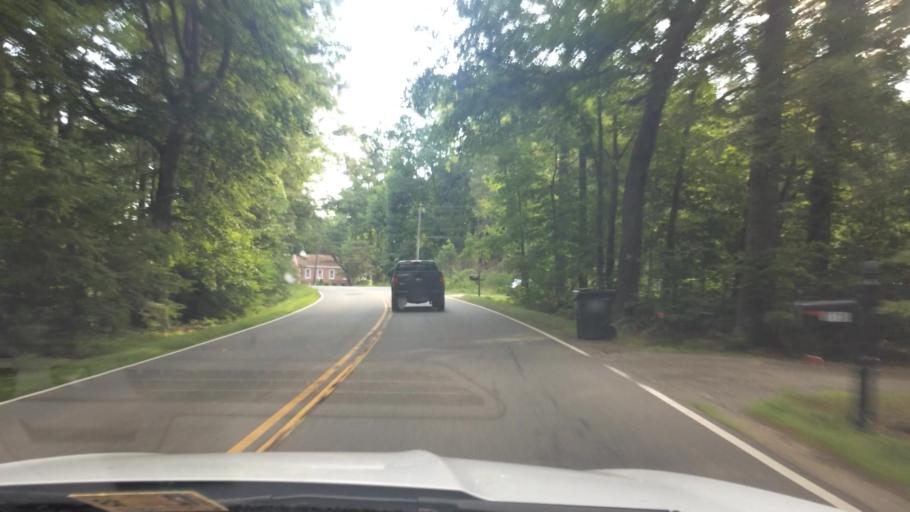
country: US
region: Virginia
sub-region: City of Williamsburg
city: Williamsburg
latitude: 37.2735
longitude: -76.6350
